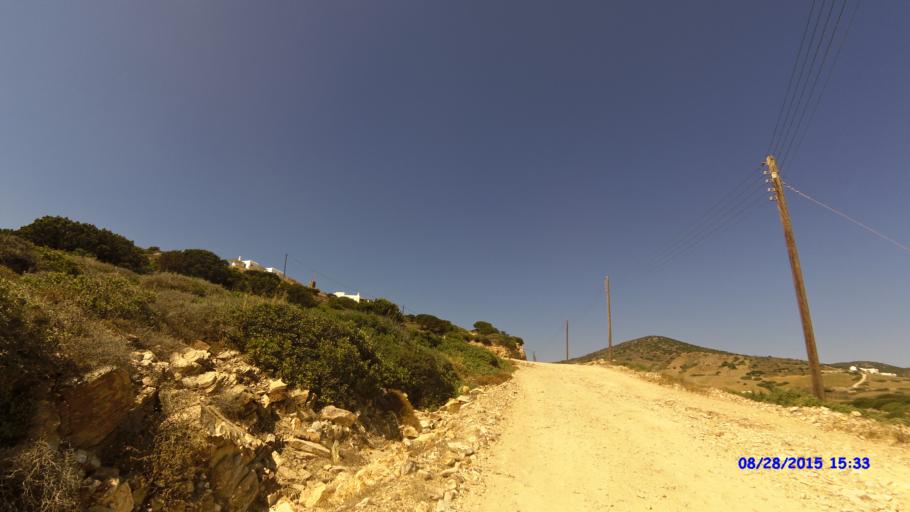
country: GR
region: South Aegean
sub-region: Nomos Kykladon
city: Antiparos
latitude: 36.9801
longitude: 25.0279
